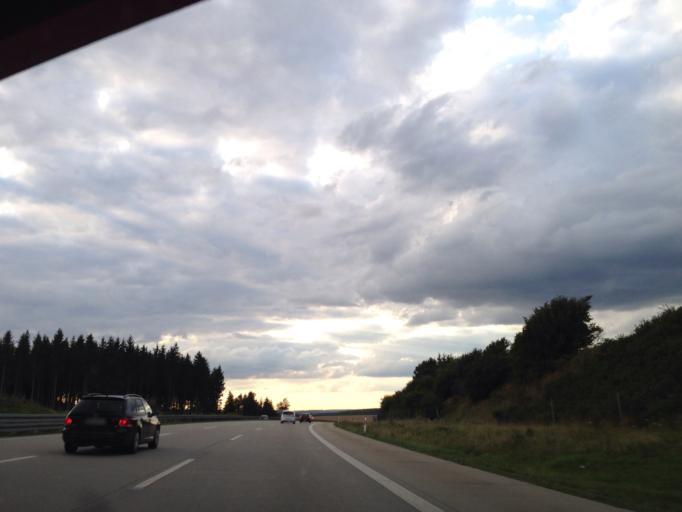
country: DE
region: Thuringia
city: Tanna
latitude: 50.4960
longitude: 11.7981
